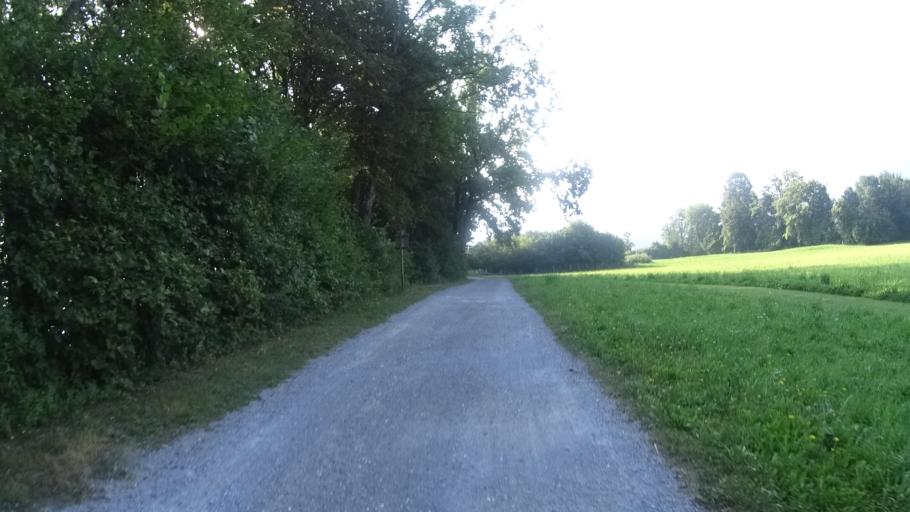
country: AT
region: Carinthia
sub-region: Politischer Bezirk Klagenfurt Land
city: Ludmannsdorf
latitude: 46.5319
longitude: 14.1383
